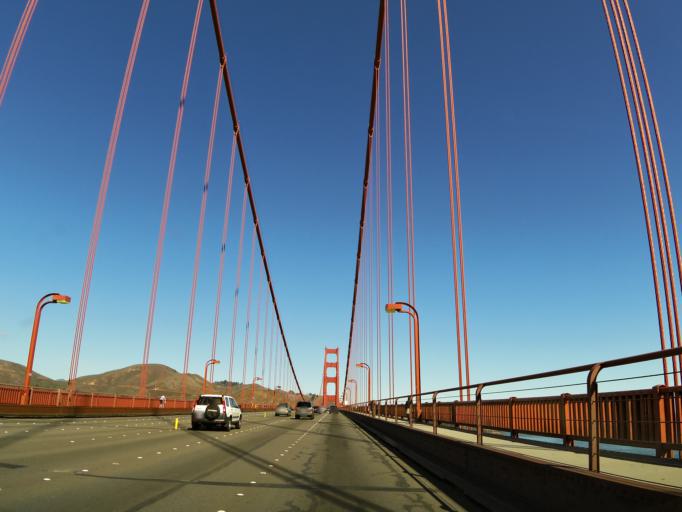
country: US
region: California
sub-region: Marin County
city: Sausalito
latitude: 37.8155
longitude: -122.4780
